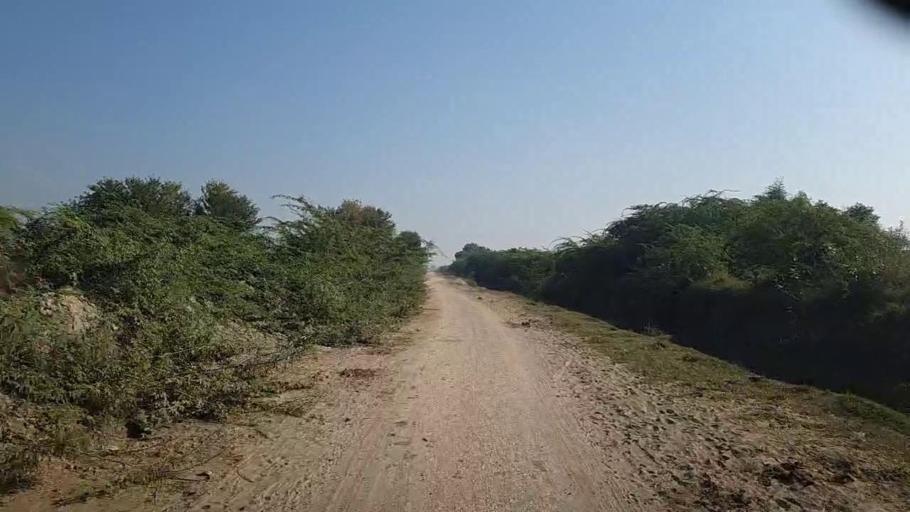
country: PK
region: Sindh
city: Darya Khan Marri
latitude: 26.7056
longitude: 68.3293
